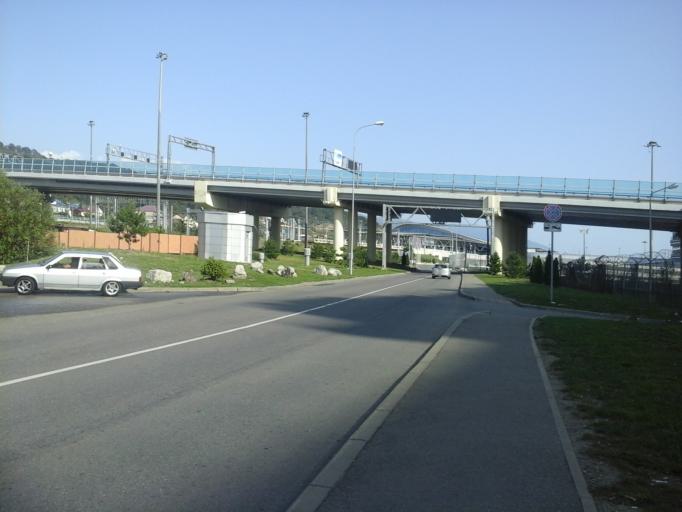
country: RU
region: Krasnodarskiy
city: Adler
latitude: 43.4136
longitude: 39.9670
